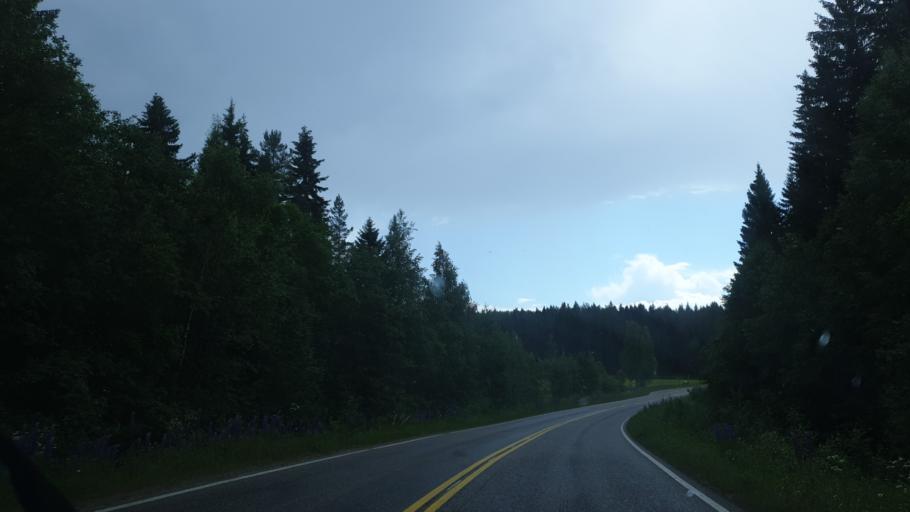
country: FI
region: Northern Savo
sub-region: Kuopio
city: Vehmersalmi
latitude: 62.9209
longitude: 27.9180
